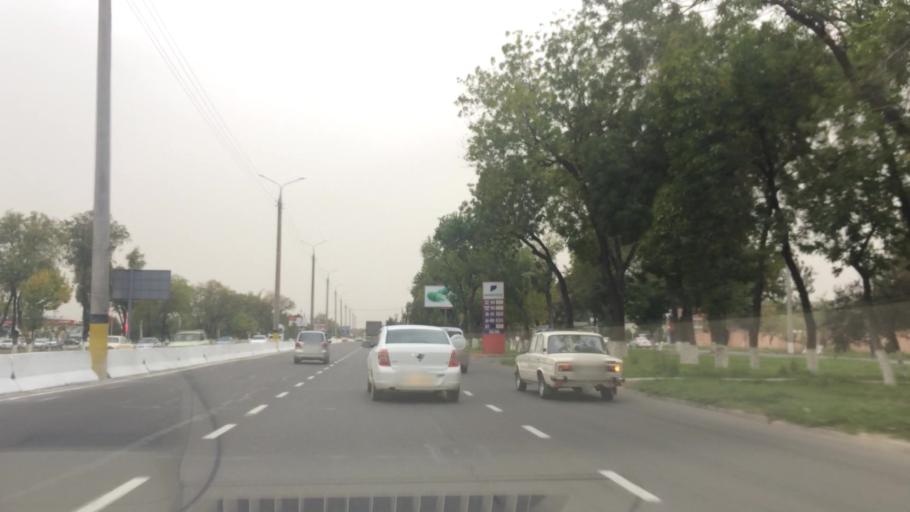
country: UZ
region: Toshkent
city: Salor
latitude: 41.3125
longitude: 69.3485
